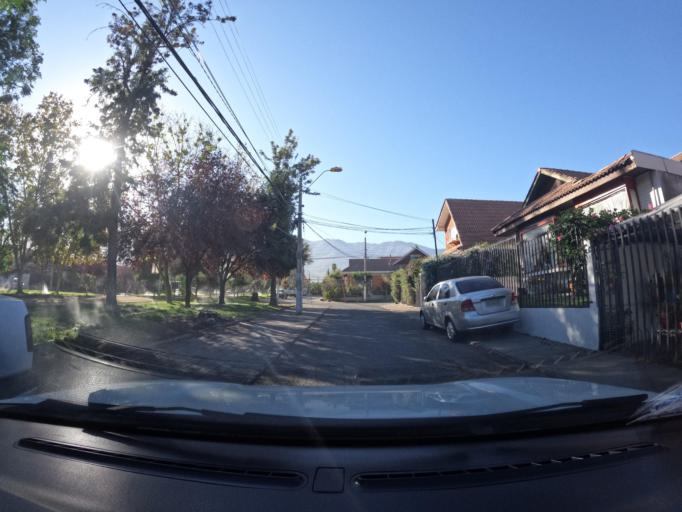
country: CL
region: Santiago Metropolitan
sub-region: Provincia de Santiago
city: Villa Presidente Frei, Nunoa, Santiago, Chile
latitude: -33.4783
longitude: -70.5541
